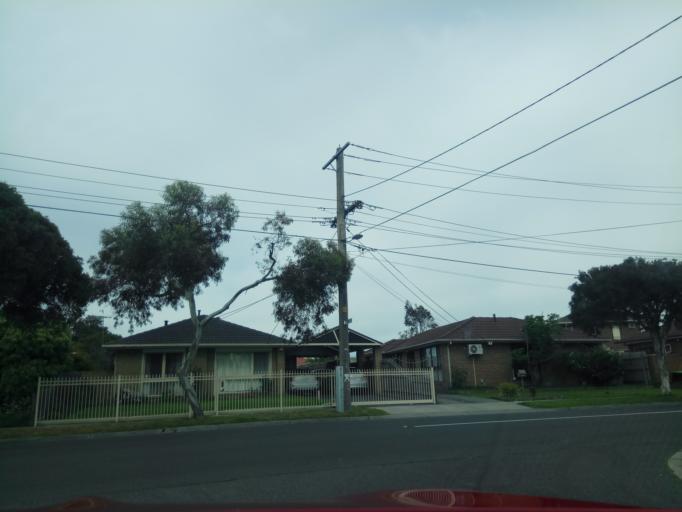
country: AU
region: Victoria
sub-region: Greater Dandenong
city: Springvale South
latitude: -37.9652
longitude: 145.1436
